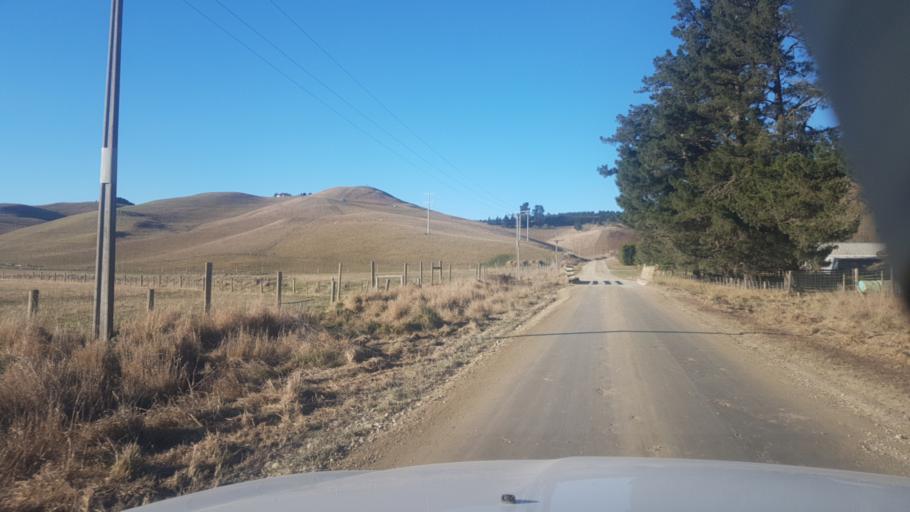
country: NZ
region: Canterbury
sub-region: Timaru District
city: Pleasant Point
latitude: -44.3434
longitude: 171.0585
